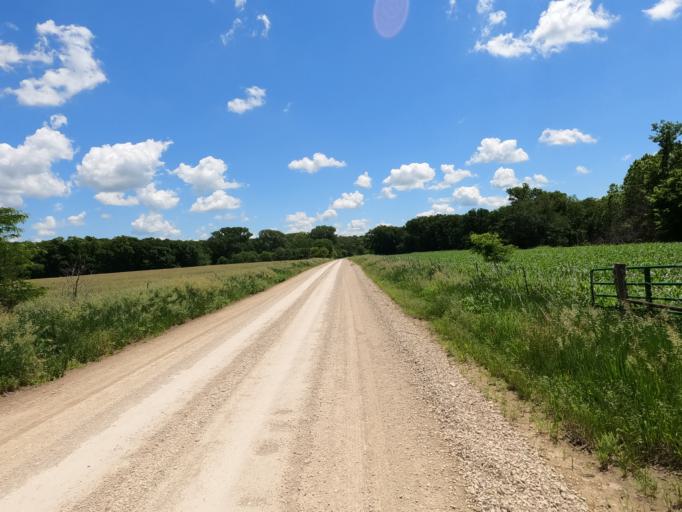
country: US
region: Kansas
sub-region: Marion County
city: Marion
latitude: 38.2454
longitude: -96.8139
